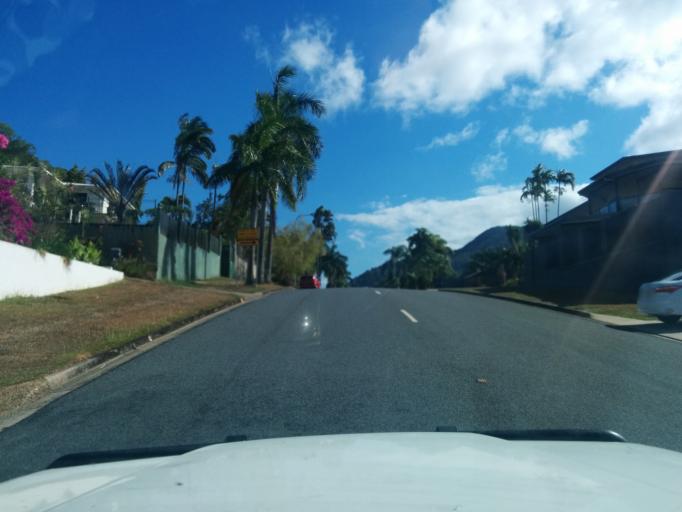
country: AU
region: Queensland
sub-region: Cairns
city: Woree
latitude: -16.9516
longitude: 145.7332
